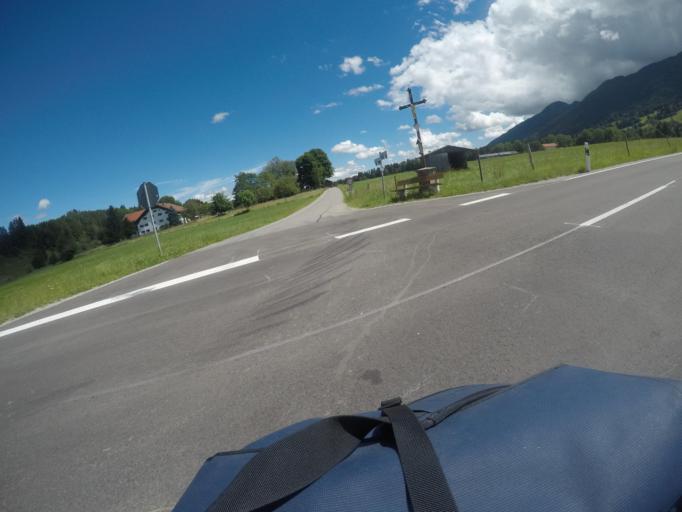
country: DE
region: Bavaria
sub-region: Swabia
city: Halblech
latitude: 47.6279
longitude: 10.8089
